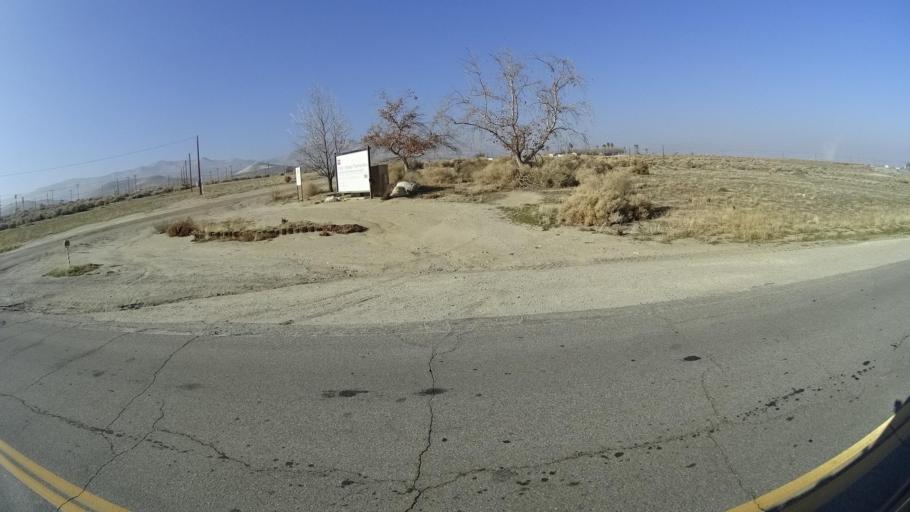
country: US
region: California
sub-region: Kern County
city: Taft Heights
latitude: 35.1816
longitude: -119.5502
